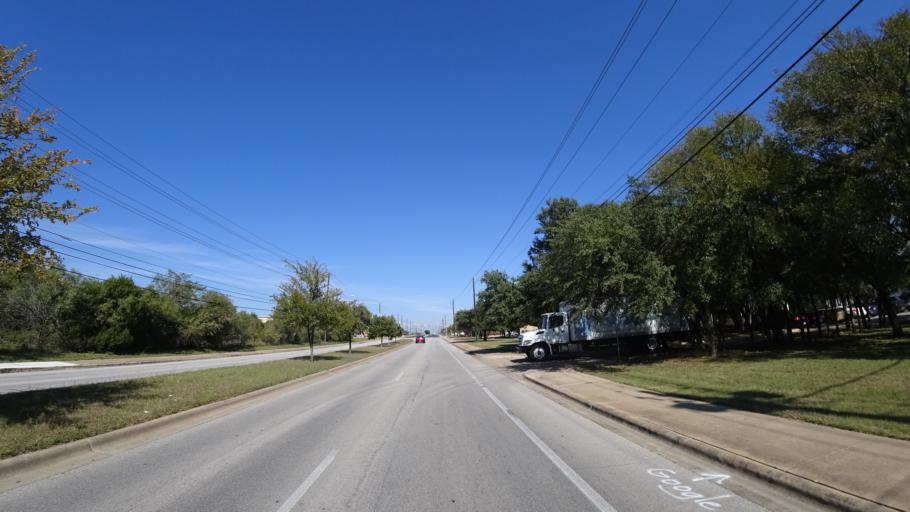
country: US
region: Texas
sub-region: Travis County
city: Shady Hollow
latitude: 30.1891
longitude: -97.8462
